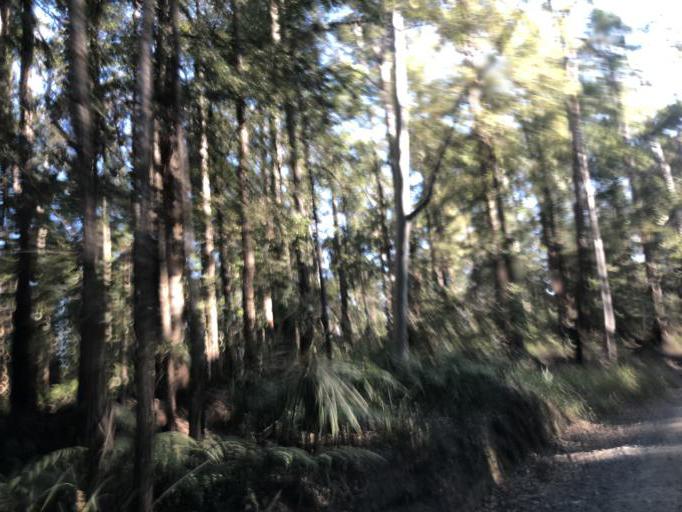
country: AU
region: New South Wales
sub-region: Bellingen
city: Bellingen
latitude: -30.4338
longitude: 152.8379
